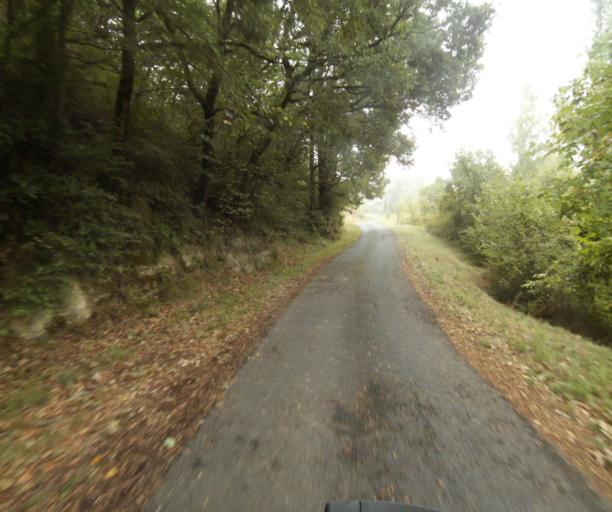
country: FR
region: Midi-Pyrenees
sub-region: Departement de la Haute-Garonne
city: Villemur-sur-Tarn
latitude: 43.8898
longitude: 1.4843
